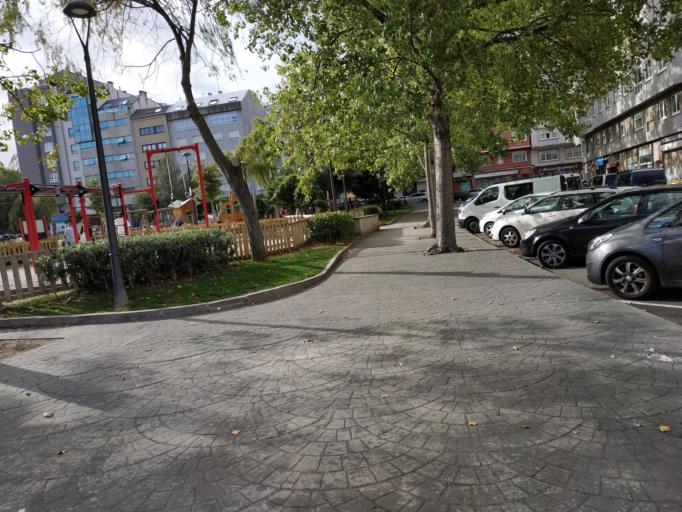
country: ES
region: Galicia
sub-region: Provincia da Coruna
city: A Coruna
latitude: 43.3712
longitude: -8.4201
